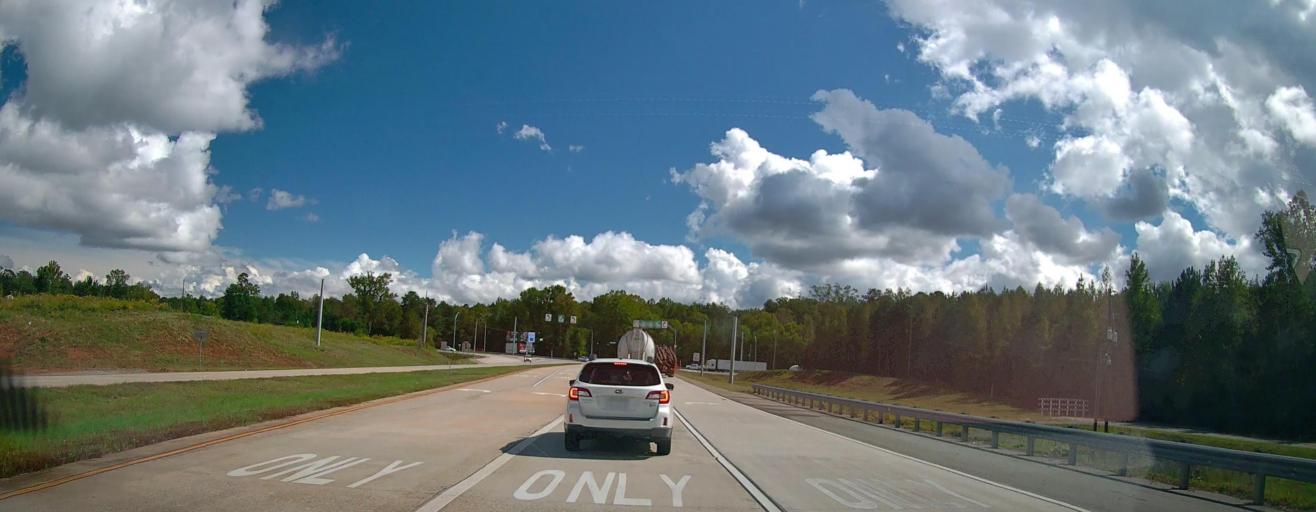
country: US
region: Georgia
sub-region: Jones County
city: Gray
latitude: 32.9893
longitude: -83.5709
